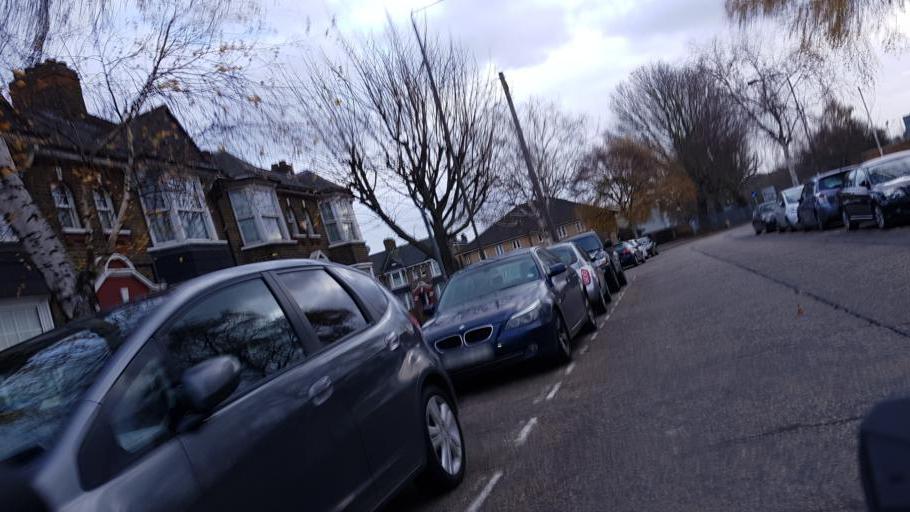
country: GB
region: England
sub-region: Greater London
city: Blackheath
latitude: 51.4917
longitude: 0.0299
